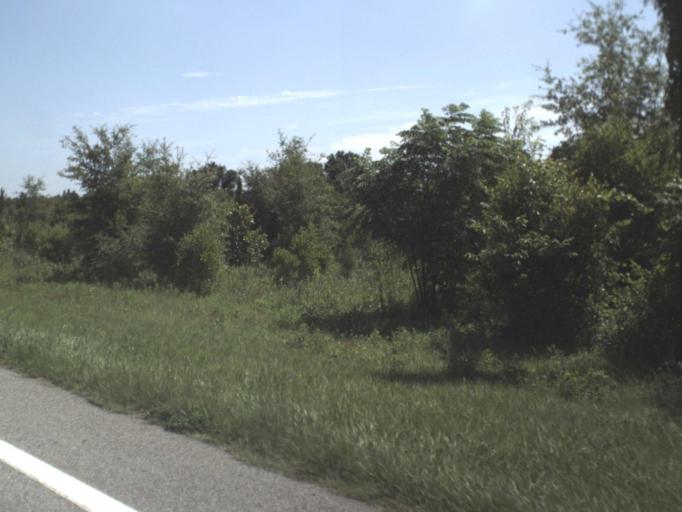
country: US
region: Florida
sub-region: Hamilton County
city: Jasper
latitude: 30.4258
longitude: -82.9337
